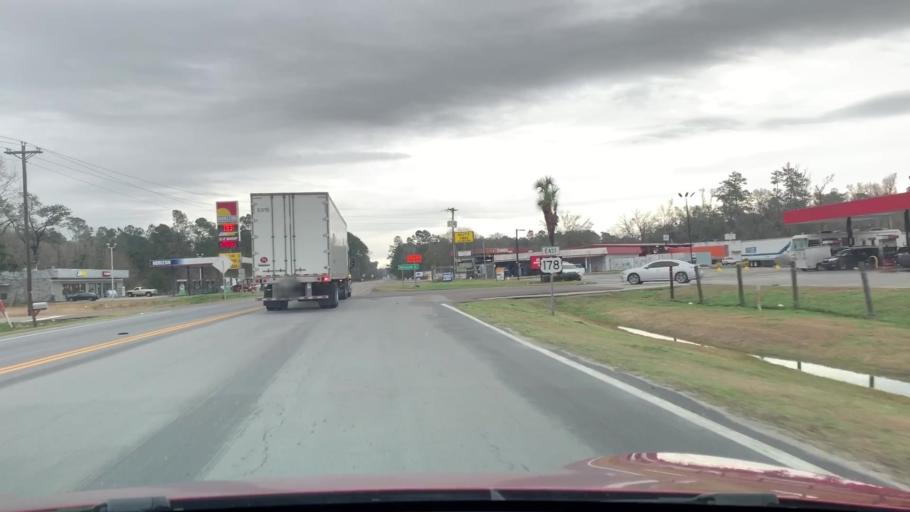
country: US
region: South Carolina
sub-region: Dorchester County
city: Saint George
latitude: 33.2703
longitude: -80.5672
